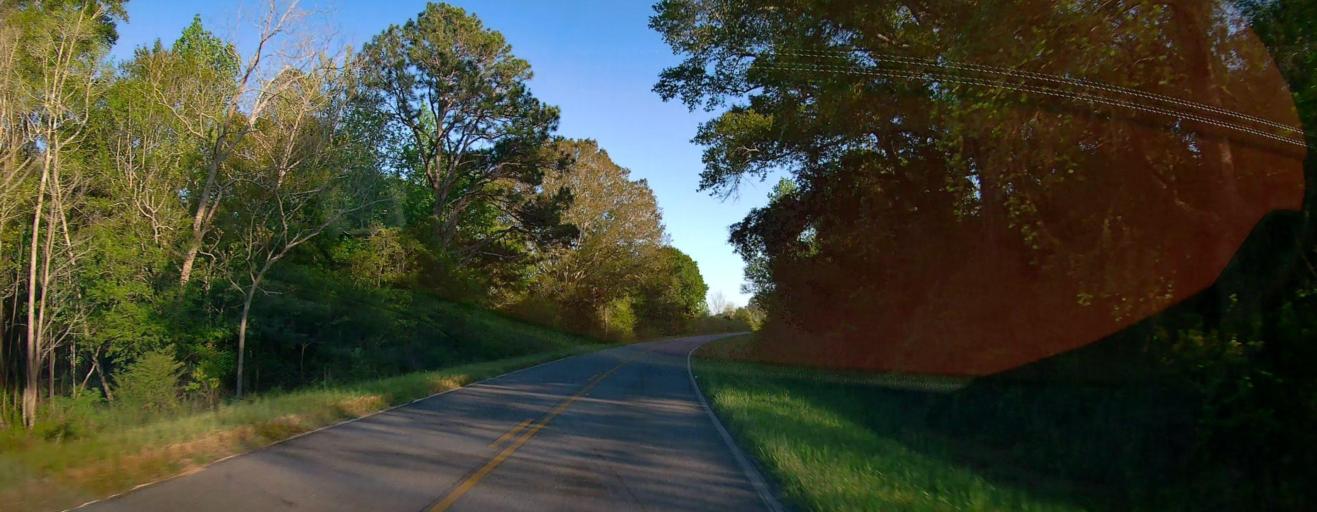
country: US
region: Georgia
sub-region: Ben Hill County
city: Fitzgerald
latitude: 31.6899
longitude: -83.2320
